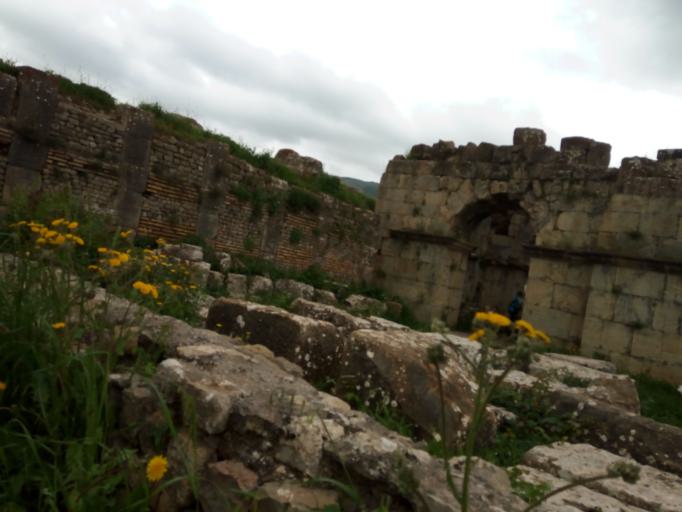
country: DZ
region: Setif
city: El Eulma
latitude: 36.3227
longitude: 5.7352
